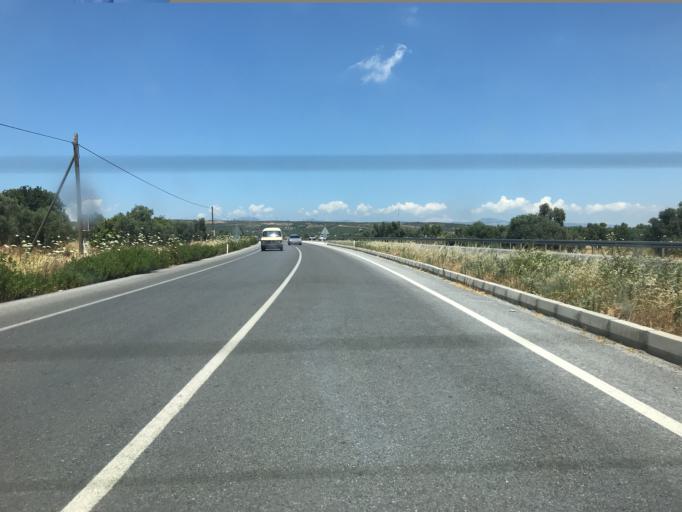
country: TR
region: Aydin
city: Akkoy
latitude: 37.4522
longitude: 27.3461
